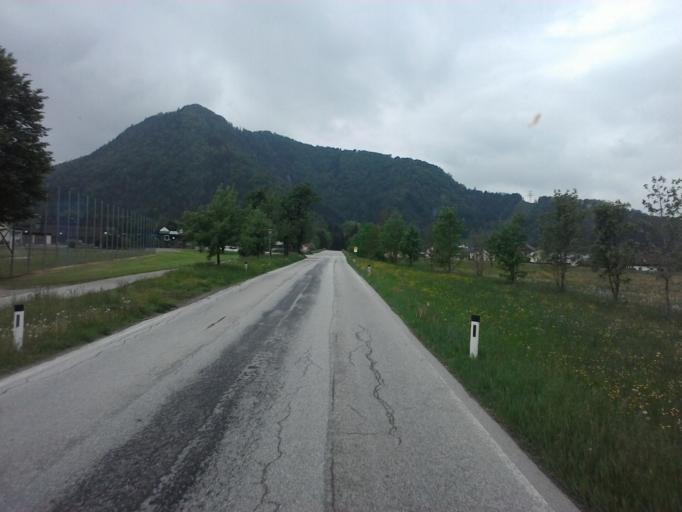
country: AT
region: Styria
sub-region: Politischer Bezirk Liezen
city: Landl
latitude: 47.6557
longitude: 14.7393
